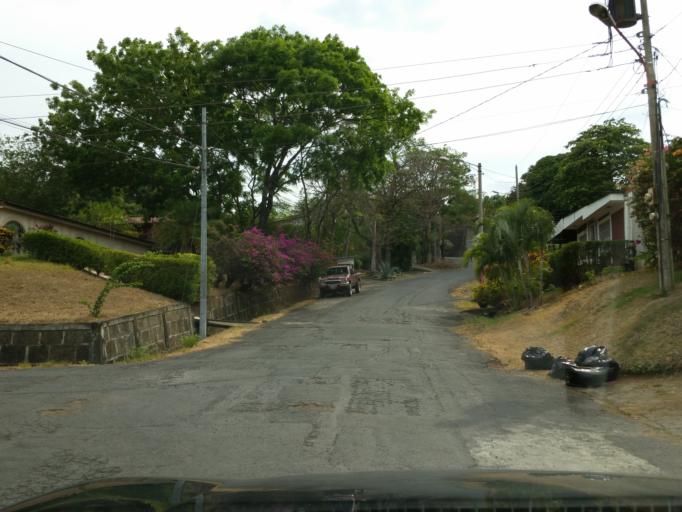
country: NI
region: Managua
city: Managua
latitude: 12.0936
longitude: -86.2436
